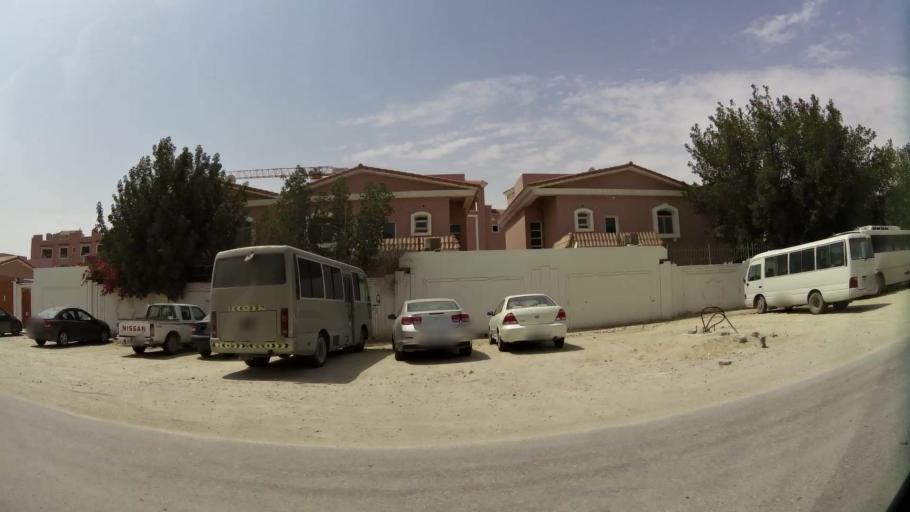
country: QA
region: Baladiyat ar Rayyan
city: Ar Rayyan
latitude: 25.3511
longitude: 51.4701
